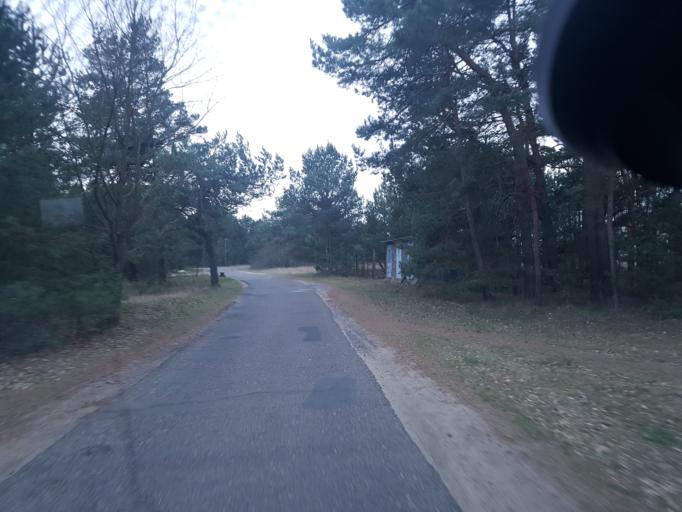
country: DE
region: Brandenburg
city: Eisenhuettenstadt
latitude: 52.1569
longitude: 14.6621
